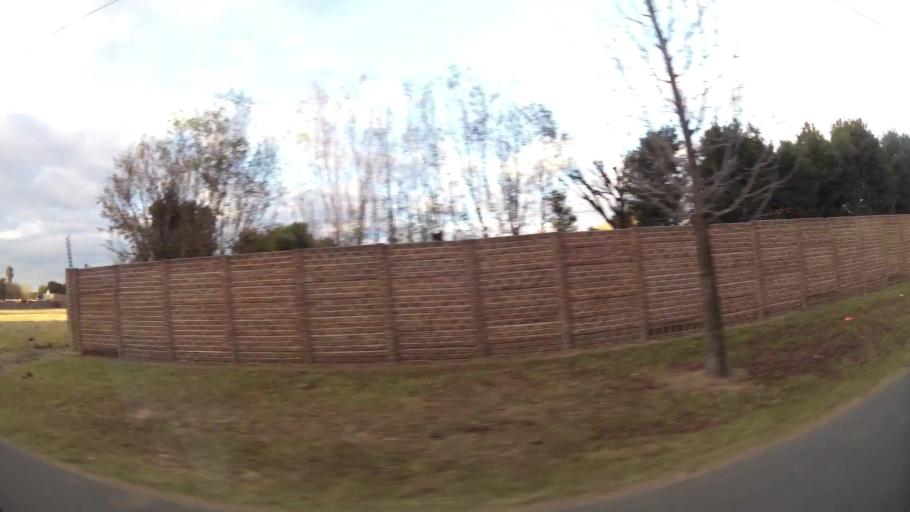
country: ZA
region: Gauteng
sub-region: City of Johannesburg Metropolitan Municipality
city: Midrand
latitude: -26.0019
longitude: 28.1517
